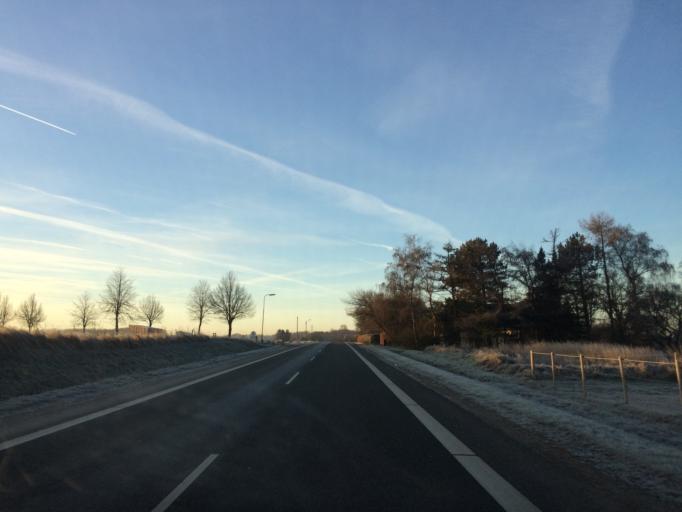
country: DK
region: South Denmark
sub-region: Odense Kommune
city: Bellinge
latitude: 55.3108
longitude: 10.3102
